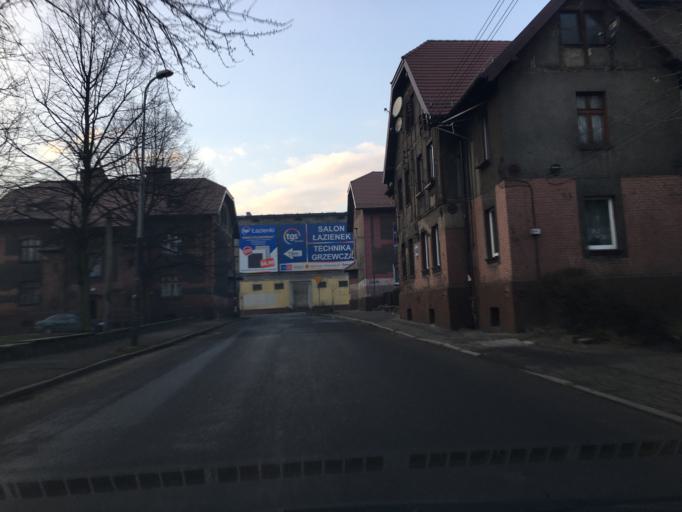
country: PL
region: Silesian Voivodeship
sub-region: Bytom
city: Bytom
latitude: 50.3400
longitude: 18.8714
